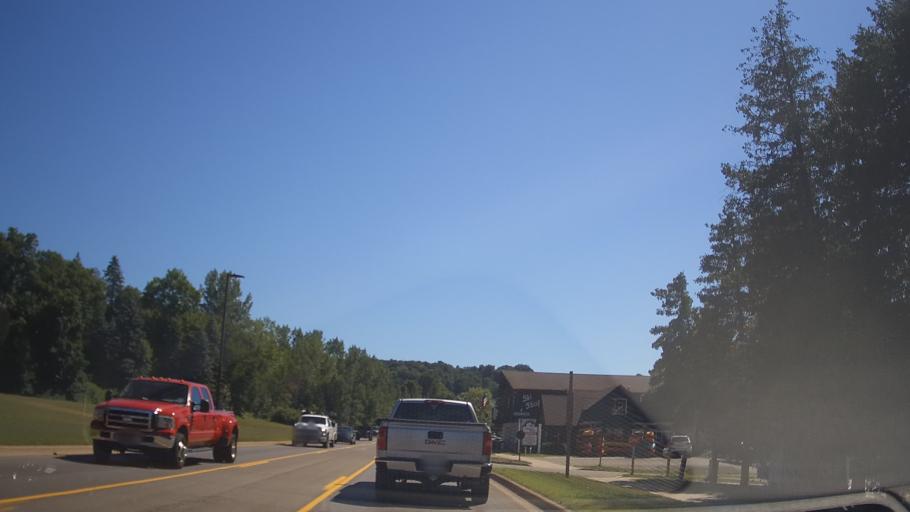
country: US
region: Michigan
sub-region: Emmet County
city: Petoskey
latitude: 45.3839
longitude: -84.9413
